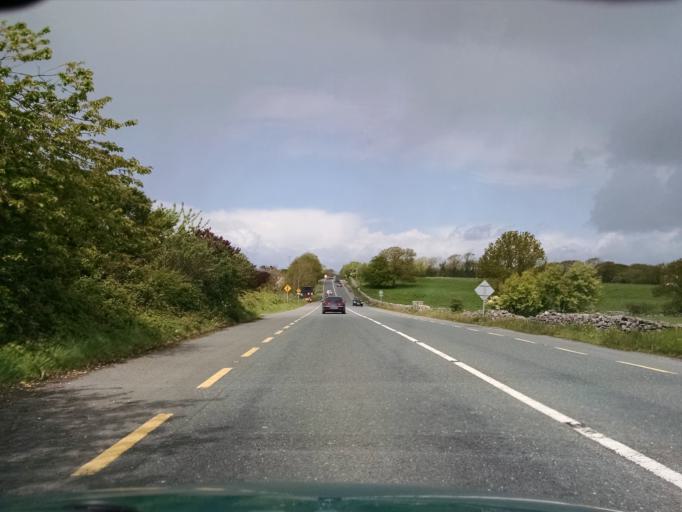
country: IE
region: Connaught
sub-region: County Galway
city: Oranmore
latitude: 53.2549
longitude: -8.9107
